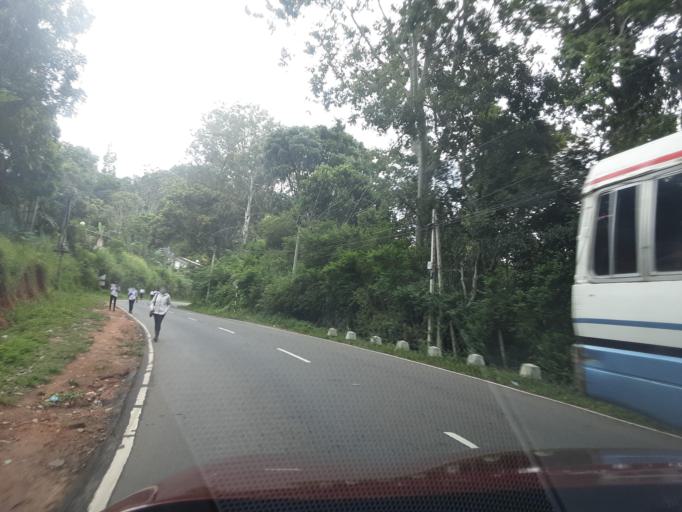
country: LK
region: Uva
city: Haputale
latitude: 6.8486
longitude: 80.9700
